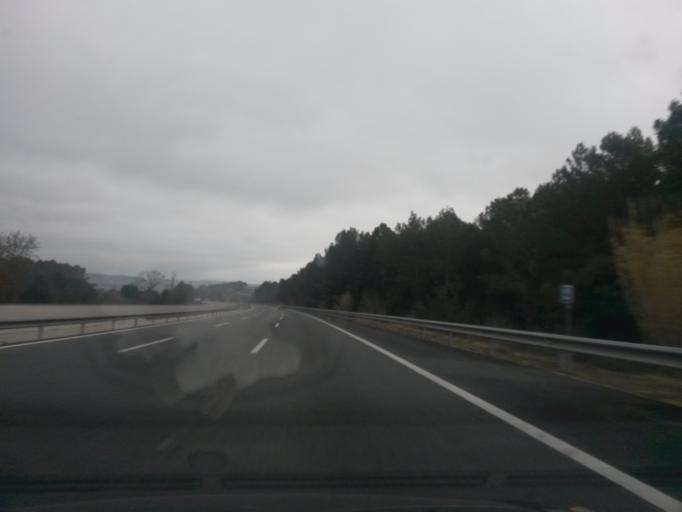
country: ES
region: Catalonia
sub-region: Provincia de Girona
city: Bascara
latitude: 42.1417
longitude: 2.9188
